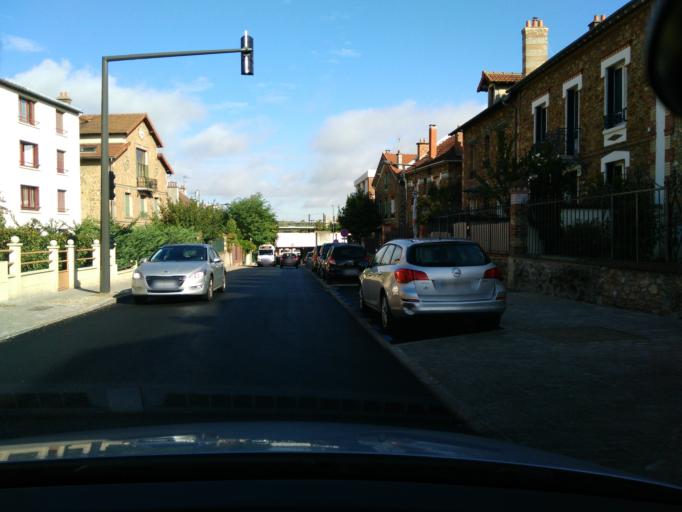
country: FR
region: Ile-de-France
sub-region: Departement de l'Essonne
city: Massy
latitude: 48.7332
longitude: 2.2732
